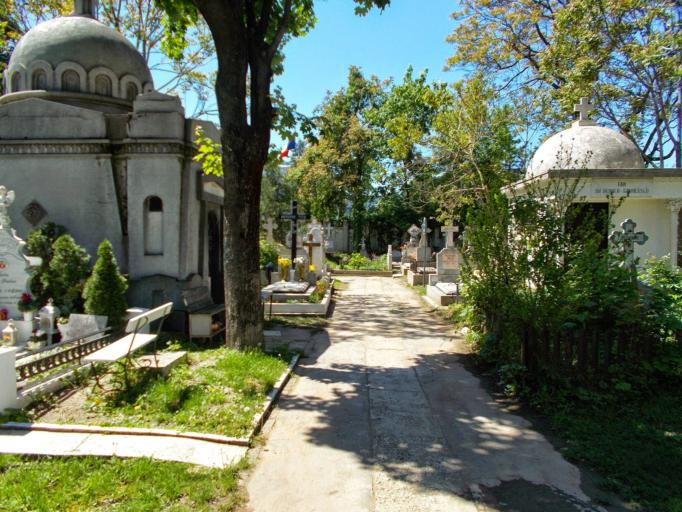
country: RO
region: Bucuresti
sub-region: Municipiul Bucuresti
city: Bucuresti
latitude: 44.4061
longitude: 26.0971
